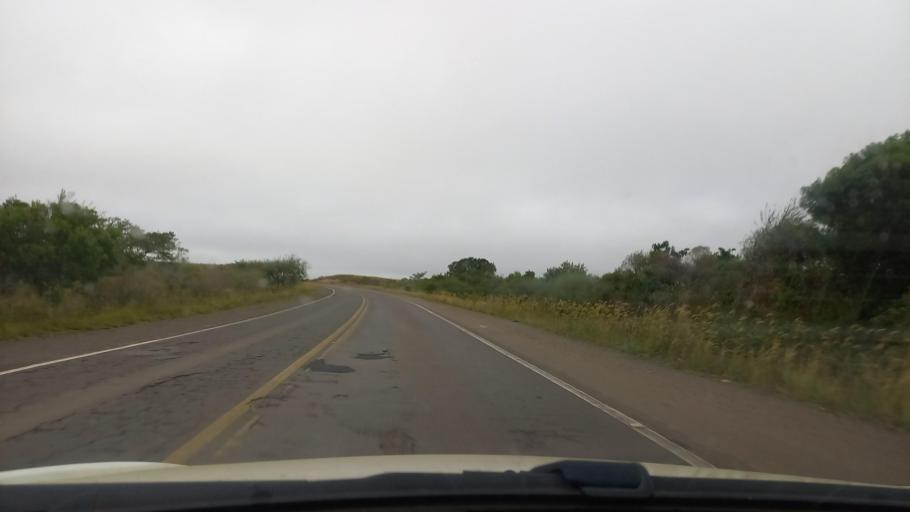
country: BR
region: Rio Grande do Sul
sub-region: Rosario Do Sul
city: Rosario do Sul
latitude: -30.1432
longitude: -54.6724
